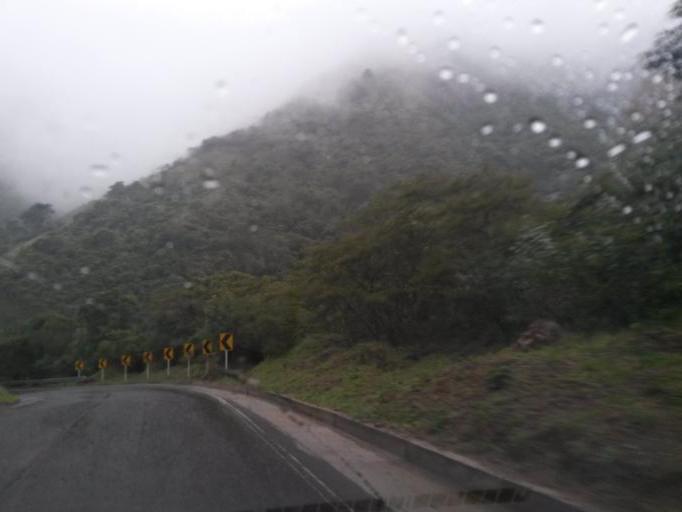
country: CO
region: Cauca
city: Popayan
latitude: 2.3739
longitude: -76.4972
